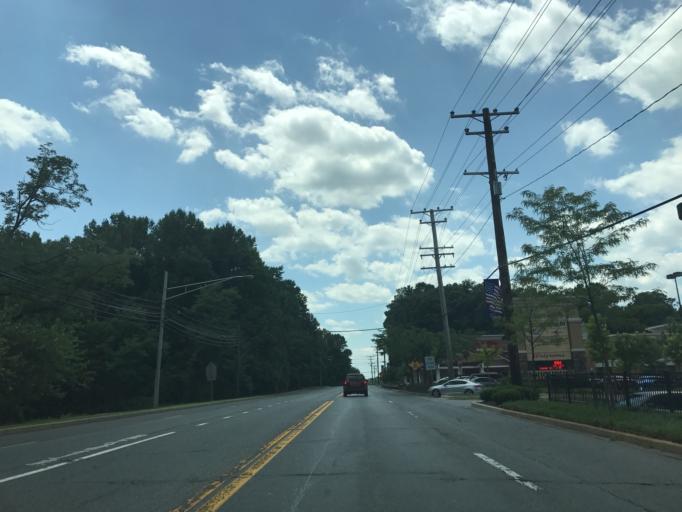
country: US
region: Maryland
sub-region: Prince George's County
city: Bowie
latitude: 38.9822
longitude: -76.7285
